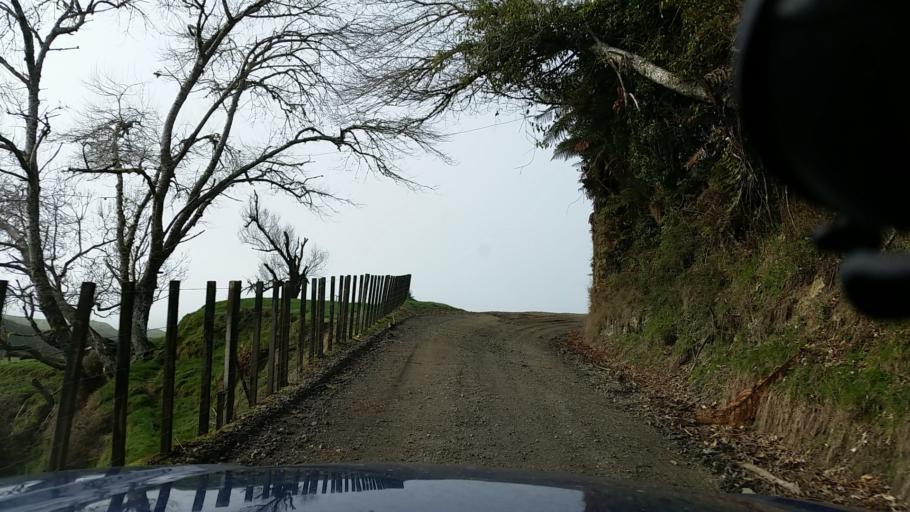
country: NZ
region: Taranaki
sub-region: New Plymouth District
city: Waitara
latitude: -38.9999
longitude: 174.7671
